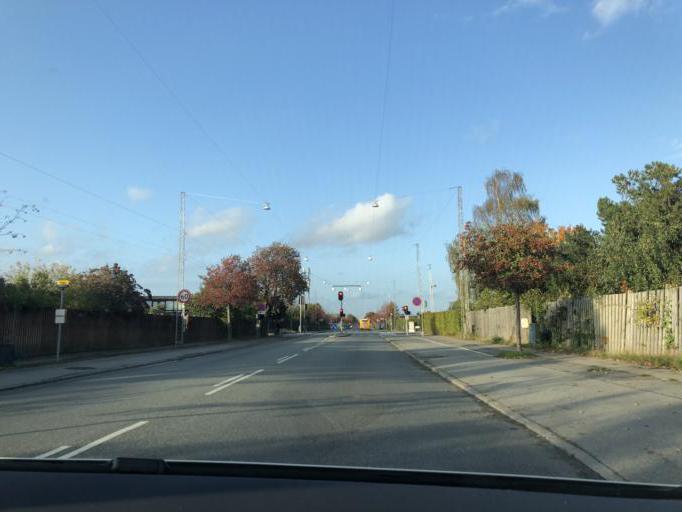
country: DK
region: Capital Region
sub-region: Tarnby Kommune
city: Tarnby
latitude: 55.6074
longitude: 12.5841
